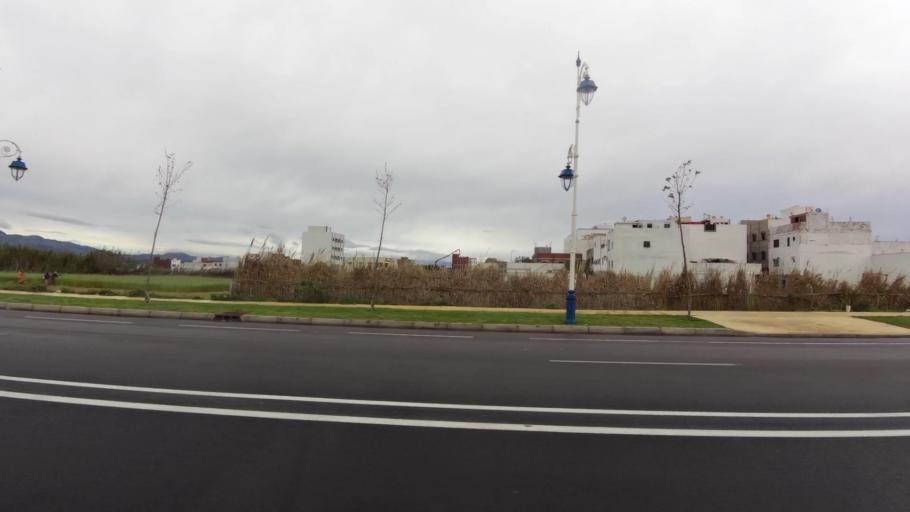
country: MA
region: Tanger-Tetouan
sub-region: Tetouan
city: Martil
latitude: 35.6294
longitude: -5.2930
